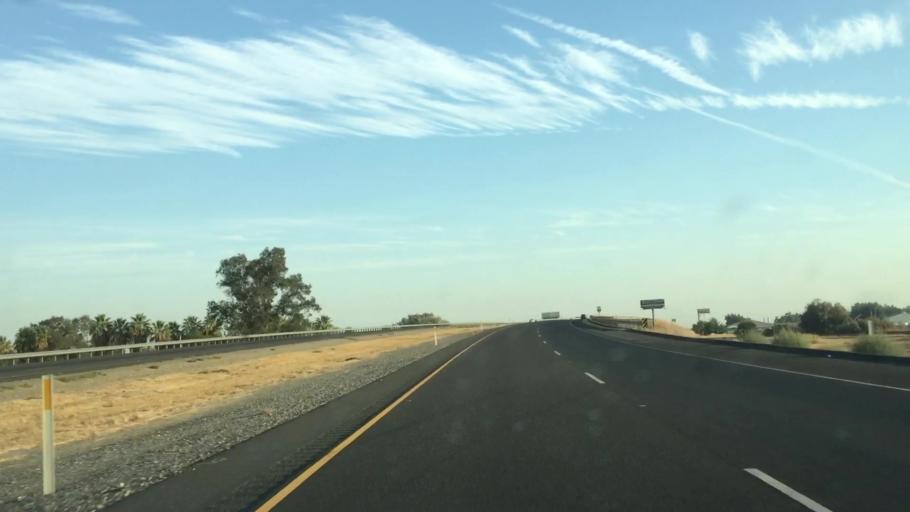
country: US
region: California
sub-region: Colusa County
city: Williams
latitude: 39.1348
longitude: -122.1358
